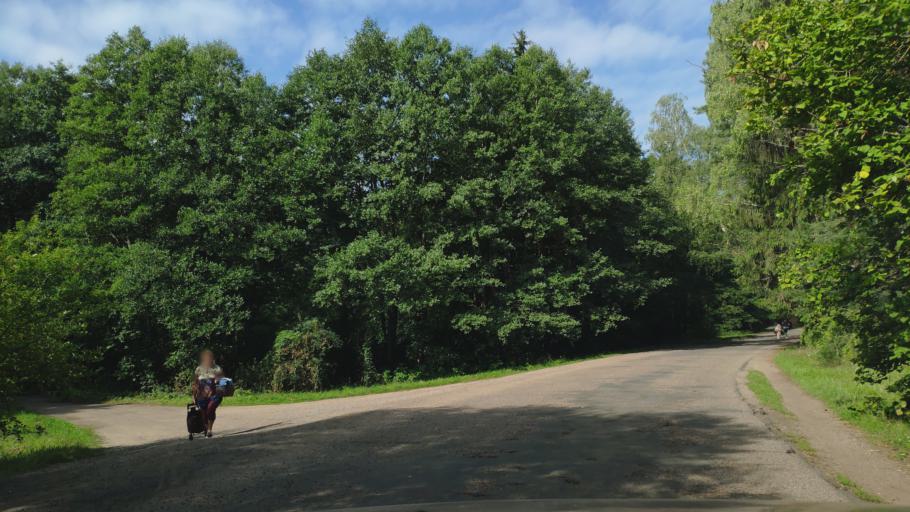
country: BY
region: Minsk
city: Zaslawye
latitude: 53.9749
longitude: 27.2903
